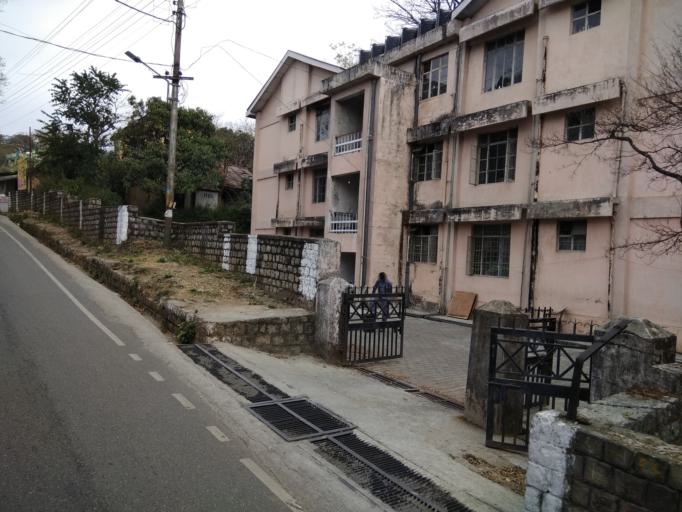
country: IN
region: Himachal Pradesh
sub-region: Kangra
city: Dharmsala
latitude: 32.2125
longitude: 76.3206
